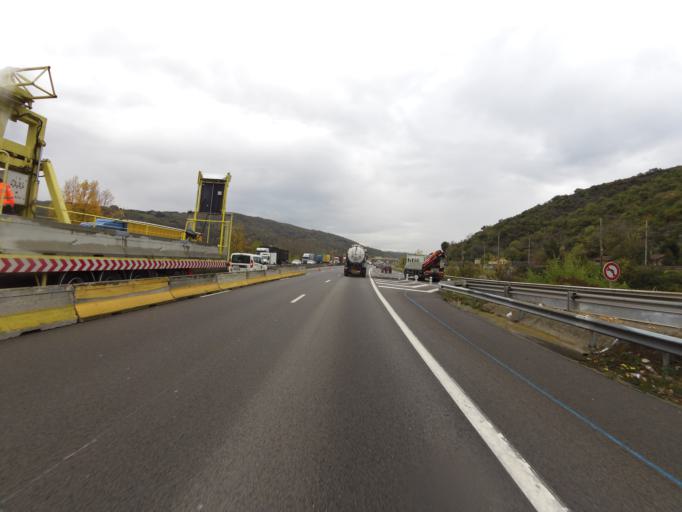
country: FR
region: Rhone-Alpes
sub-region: Departement de l'Isere
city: Seyssuel
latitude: 45.5436
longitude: 4.8442
